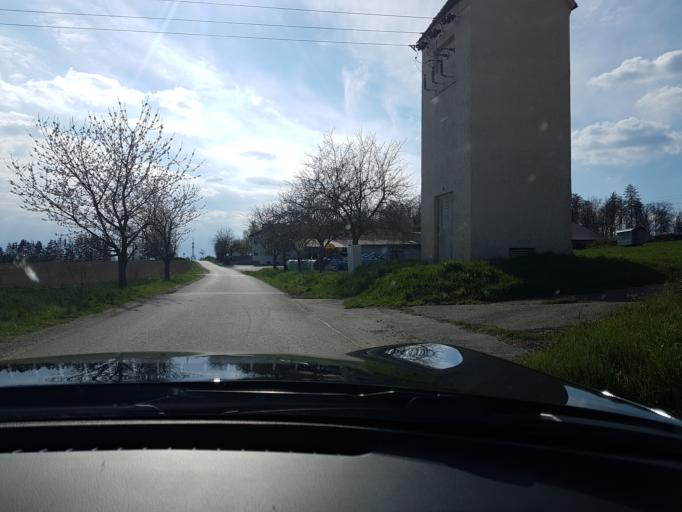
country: DE
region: Baden-Wuerttemberg
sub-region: Karlsruhe Region
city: Osterburken
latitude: 49.4198
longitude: 9.4372
